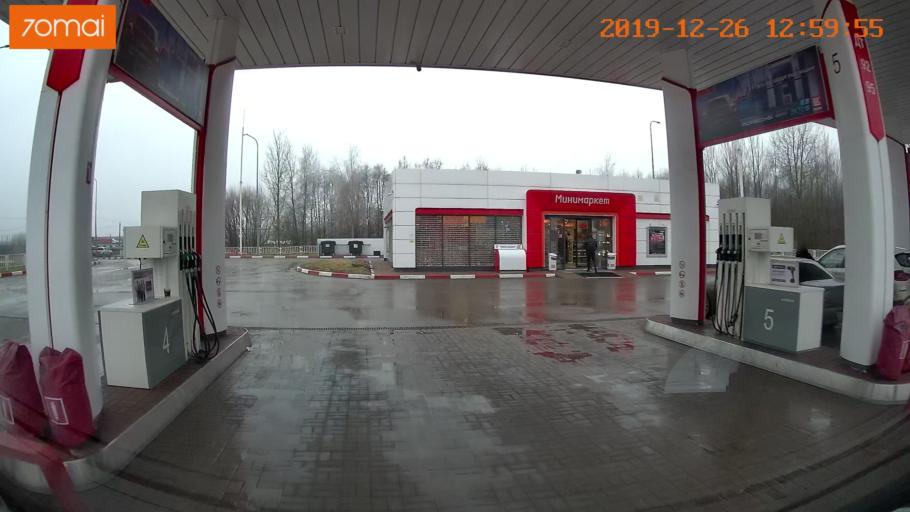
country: RU
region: Vologda
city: Cherepovets
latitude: 59.0794
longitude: 37.9184
